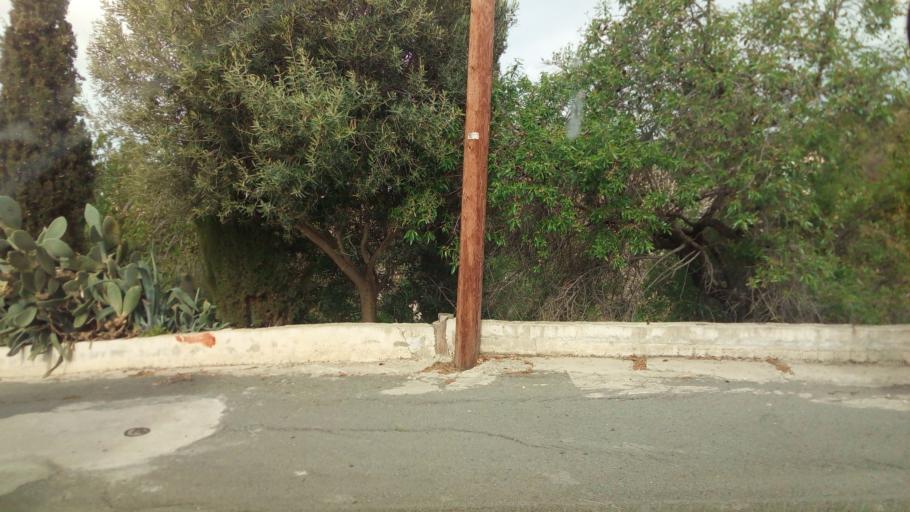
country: CY
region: Pafos
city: Mesogi
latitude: 34.7994
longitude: 32.4776
